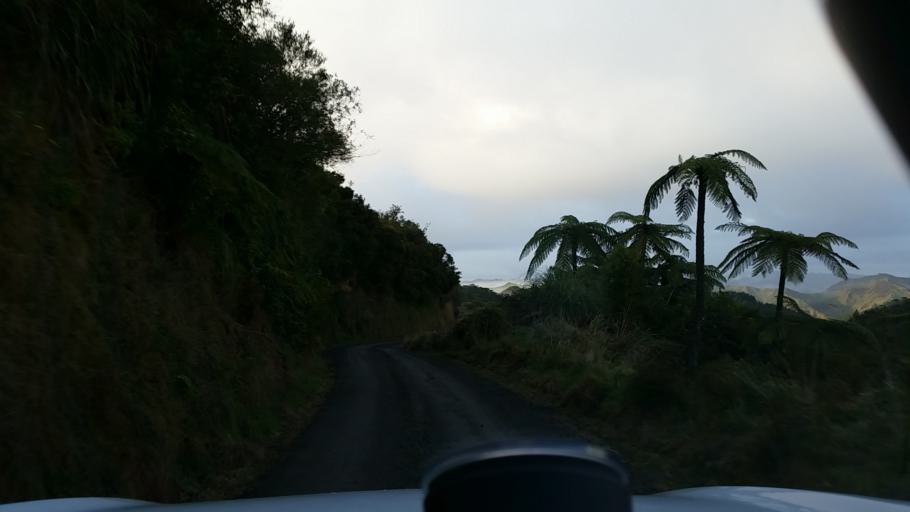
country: NZ
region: Taranaki
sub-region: South Taranaki District
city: Eltham
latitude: -39.4466
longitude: 174.4537
